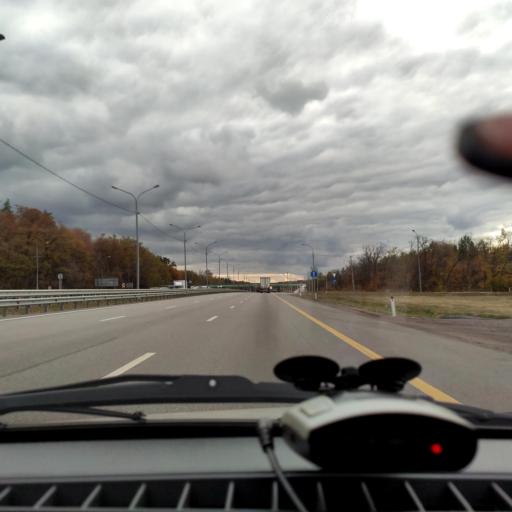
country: RU
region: Voronezj
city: Ramon'
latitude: 51.8922
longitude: 39.2177
